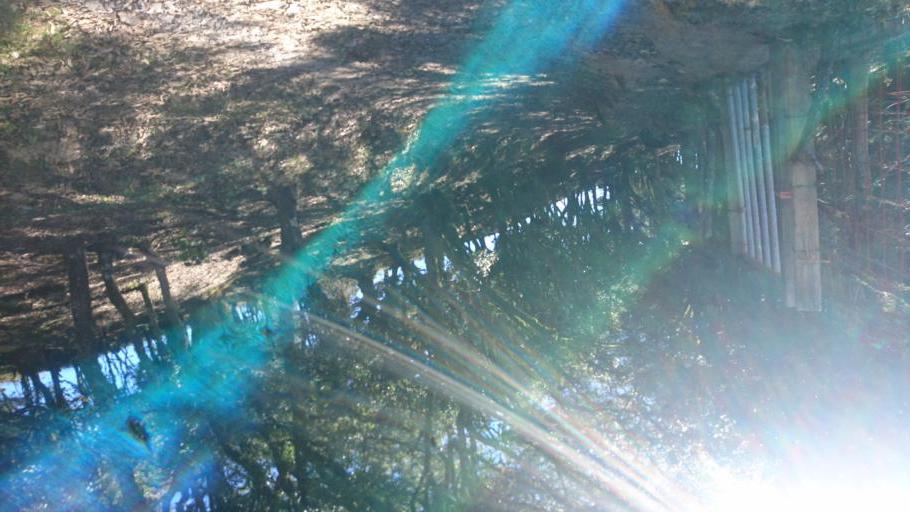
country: MX
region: San Luis Potosi
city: Zaragoza
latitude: 22.0229
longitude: -100.6192
